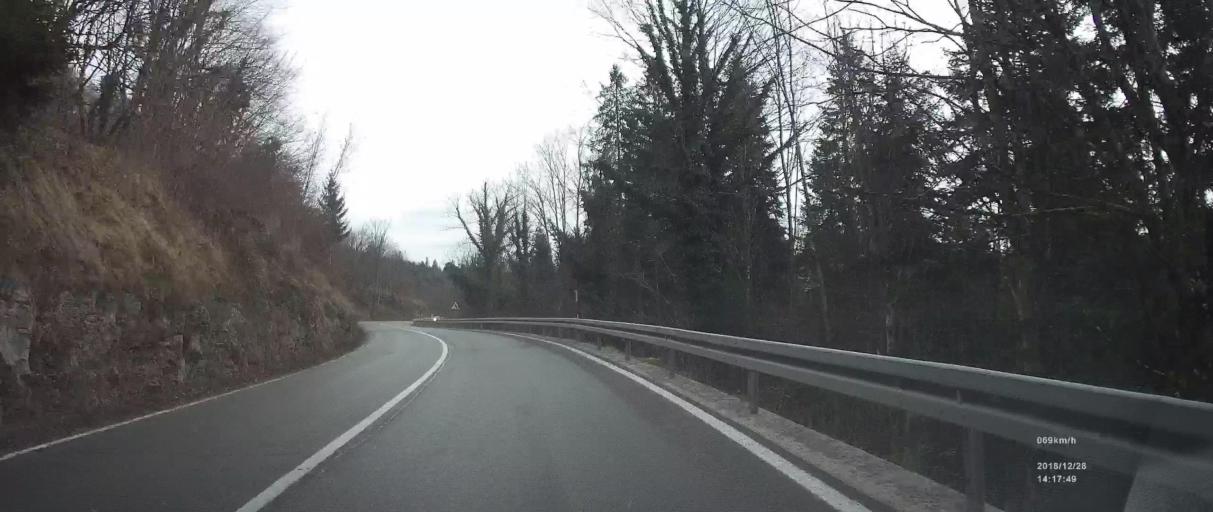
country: HR
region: Primorsko-Goranska
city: Vrbovsko
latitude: 45.4175
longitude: 15.0541
